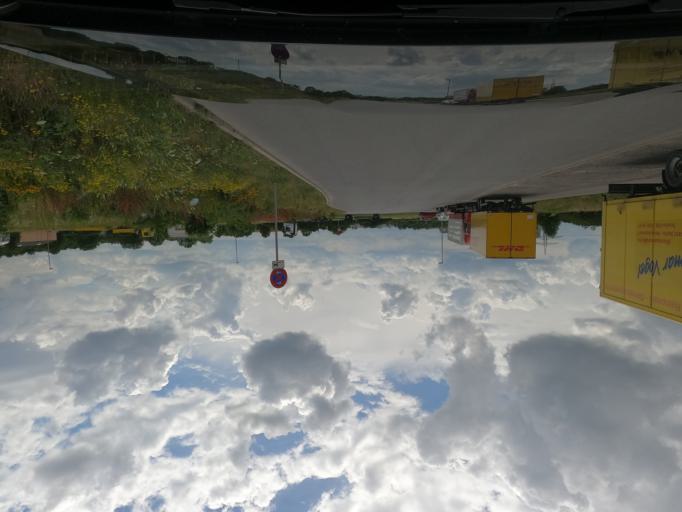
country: DE
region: Lower Saxony
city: Laatzen
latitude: 52.3646
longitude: 9.8729
